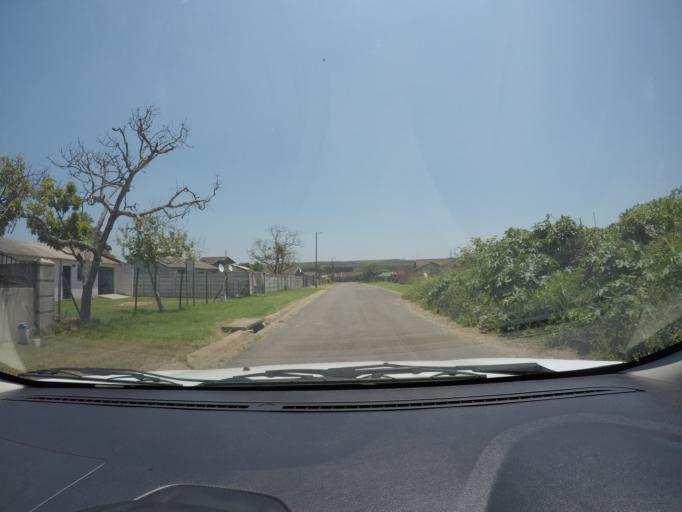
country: ZA
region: KwaZulu-Natal
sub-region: uThungulu District Municipality
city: eSikhawini
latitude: -28.8758
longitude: 31.8978
